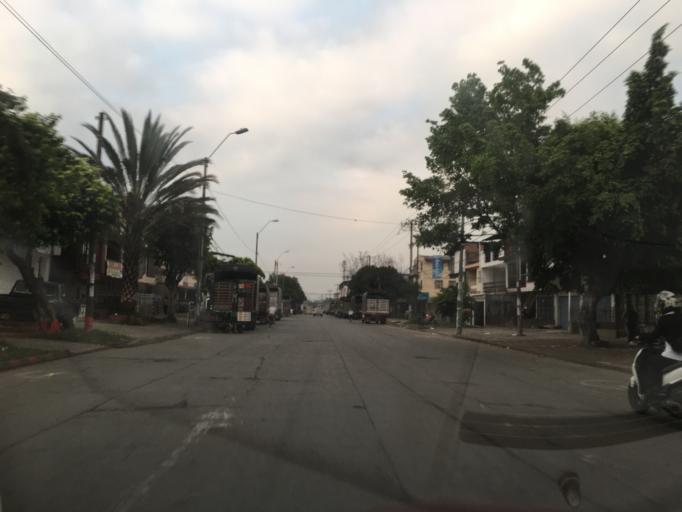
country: CO
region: Valle del Cauca
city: Cali
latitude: 3.4322
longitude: -76.5206
